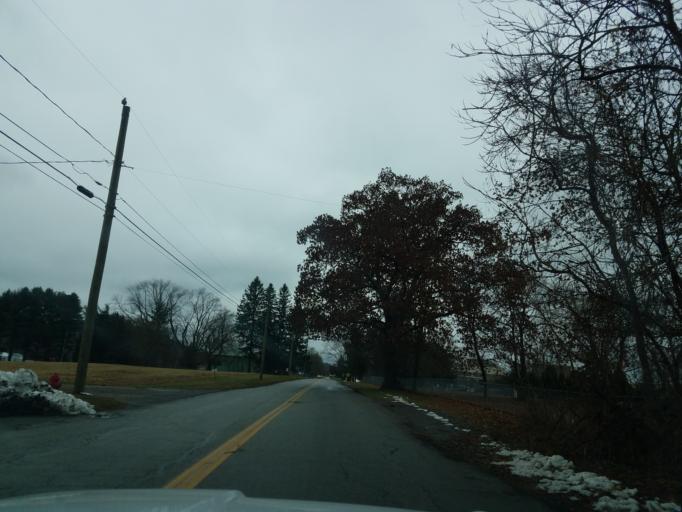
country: US
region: Connecticut
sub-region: Litchfield County
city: New Milford
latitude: 41.5620
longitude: -73.4099
